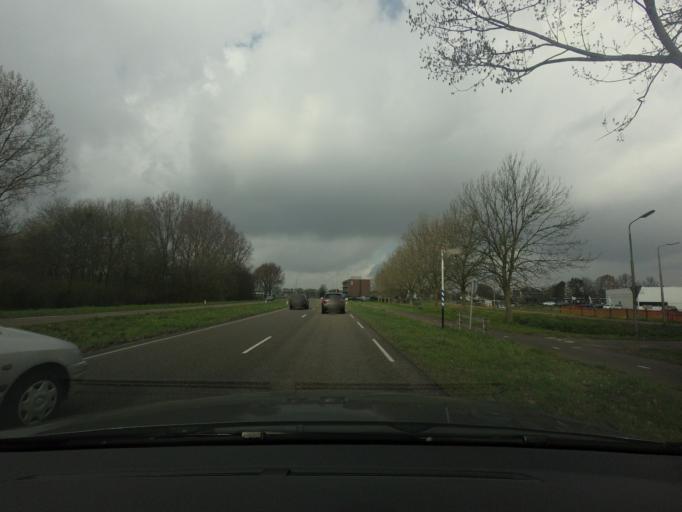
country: NL
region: North Holland
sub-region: Gemeente Aalsmeer
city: Aalsmeer
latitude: 52.2583
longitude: 4.7698
